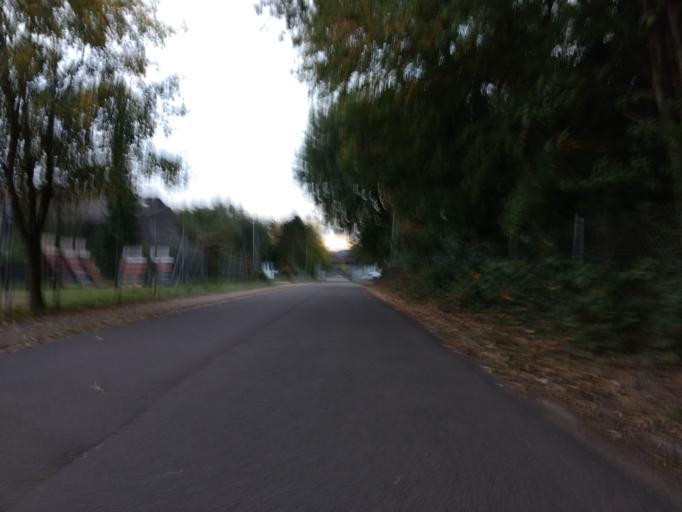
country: DE
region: Saarland
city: Beckingen
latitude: 49.3857
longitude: 6.6928
